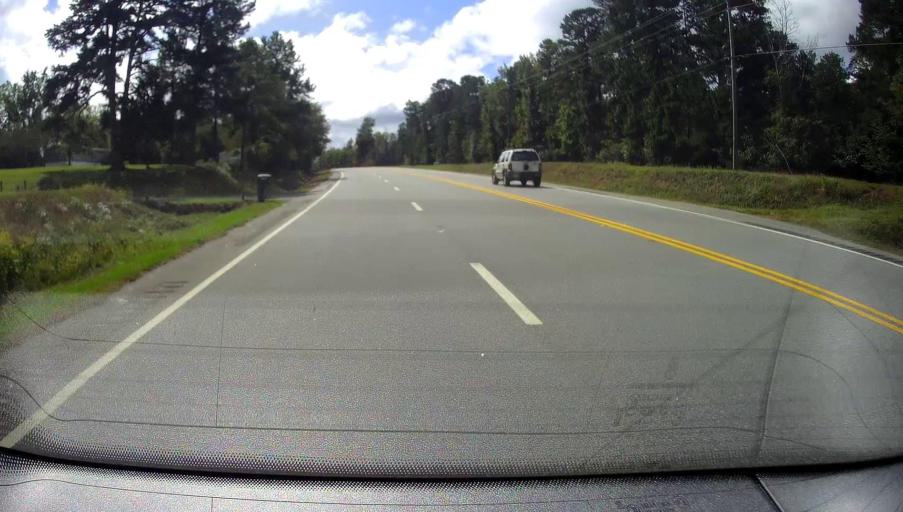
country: US
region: Georgia
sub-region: Baldwin County
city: Milledgeville
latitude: 33.0495
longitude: -83.2915
